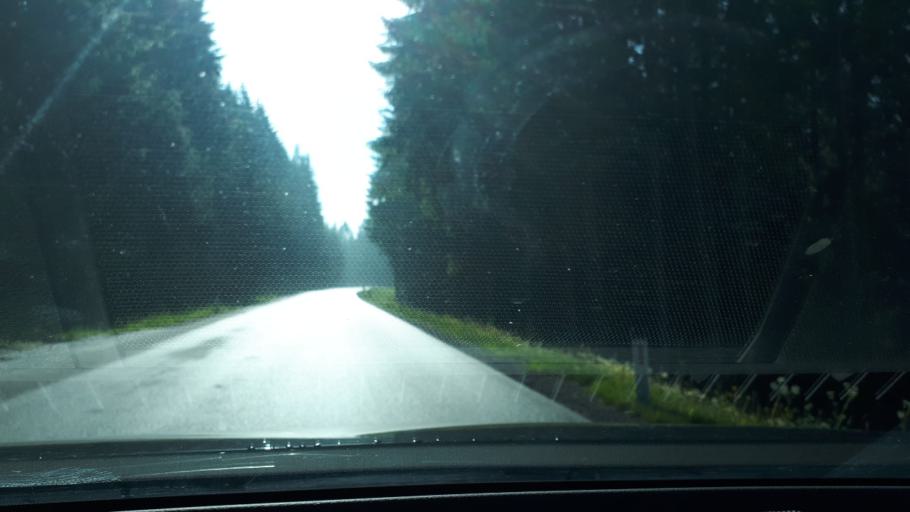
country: AT
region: Styria
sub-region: Politischer Bezirk Voitsberg
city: Pack
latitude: 46.9311
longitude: 14.9866
